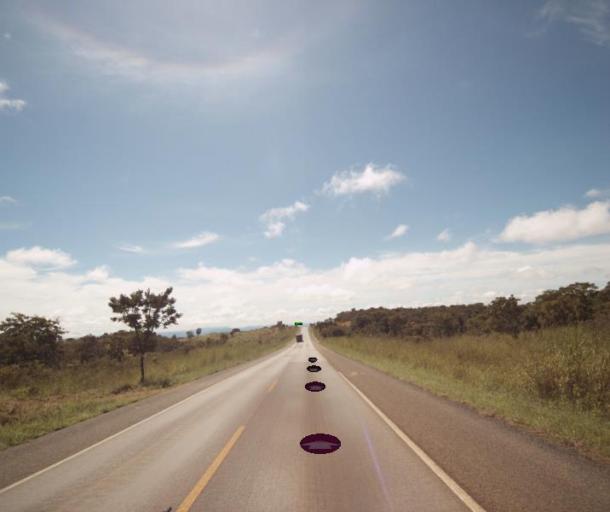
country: BR
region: Goias
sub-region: Padre Bernardo
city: Padre Bernardo
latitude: -15.1974
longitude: -48.4463
